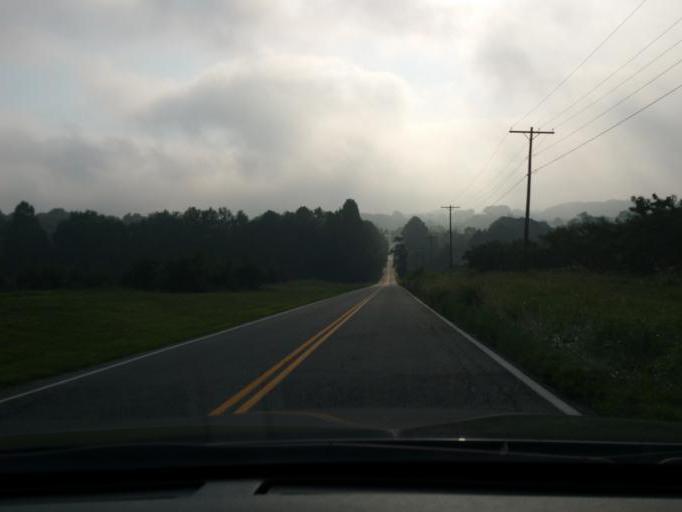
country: US
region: Maryland
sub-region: Cecil County
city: Rising Sun
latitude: 39.6716
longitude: -76.1092
